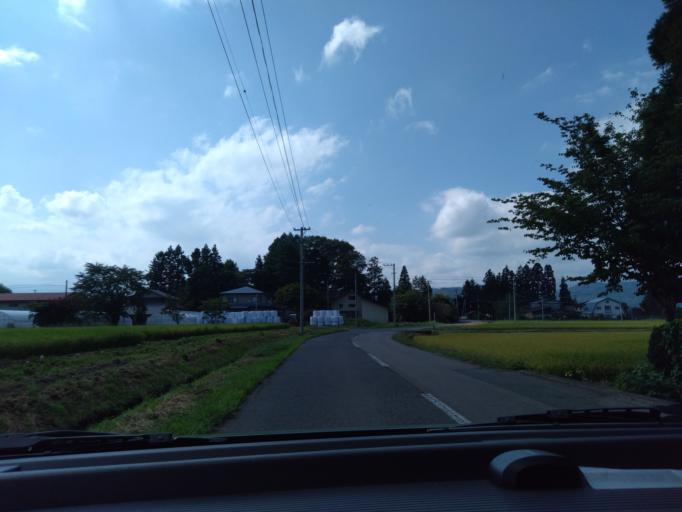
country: JP
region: Iwate
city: Shizukuishi
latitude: 39.6847
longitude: 140.9538
